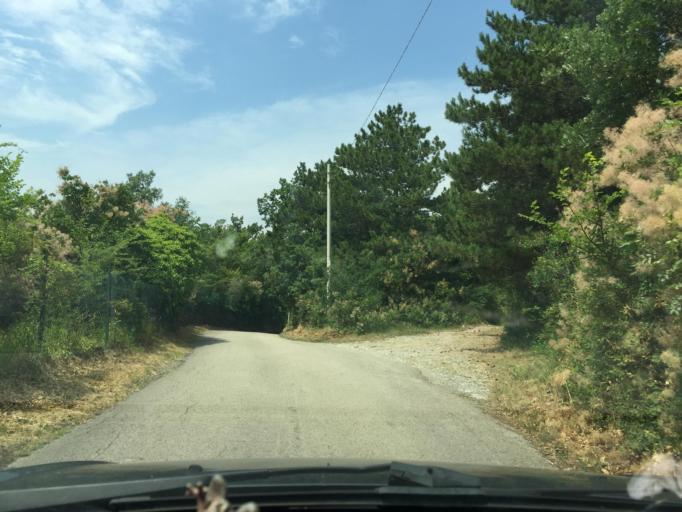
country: IT
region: Friuli Venezia Giulia
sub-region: Provincia di Trieste
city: Domio
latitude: 45.6005
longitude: 13.8179
